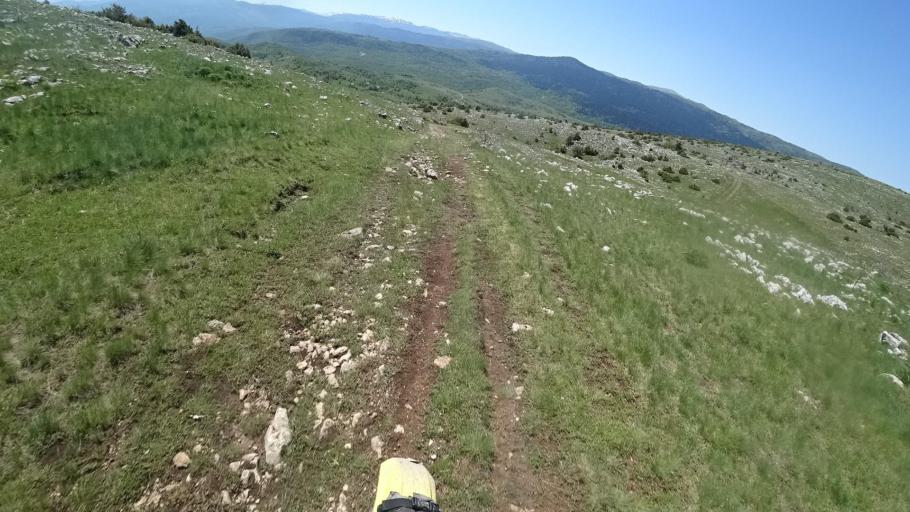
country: BA
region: Federation of Bosnia and Herzegovina
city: Rumboci
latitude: 43.8386
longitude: 17.4438
